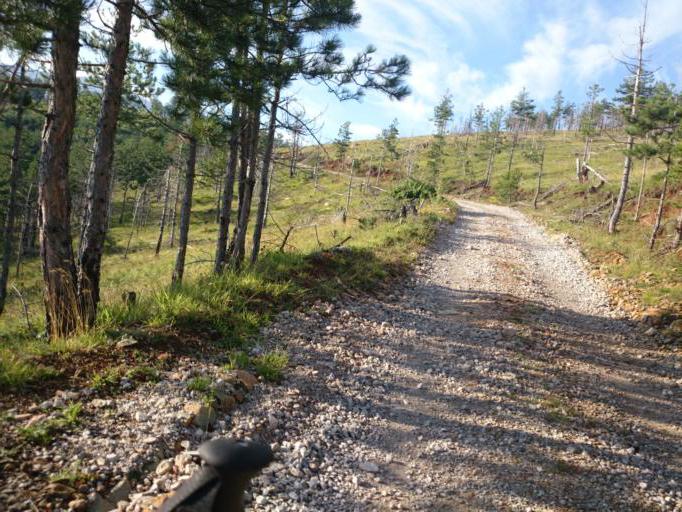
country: AL
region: Diber
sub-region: Rrethi i Dibres
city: Fushe-Lure
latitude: 41.8073
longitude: 20.2142
